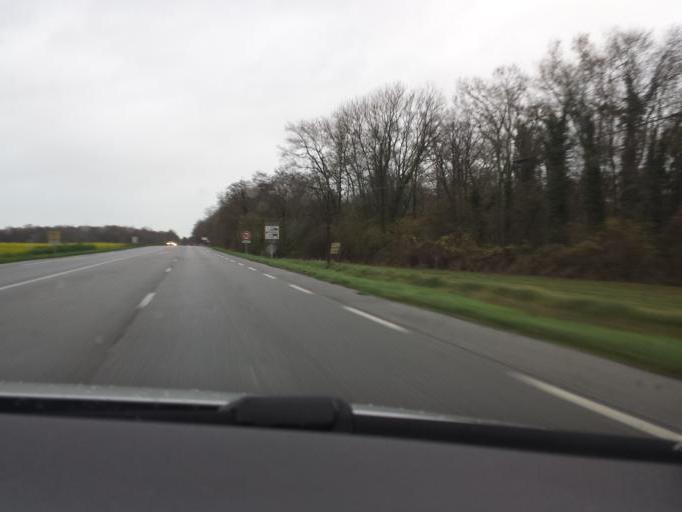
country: FR
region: Haute-Normandie
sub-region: Departement de l'Eure
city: Menilles
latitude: 49.0116
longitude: 1.3235
